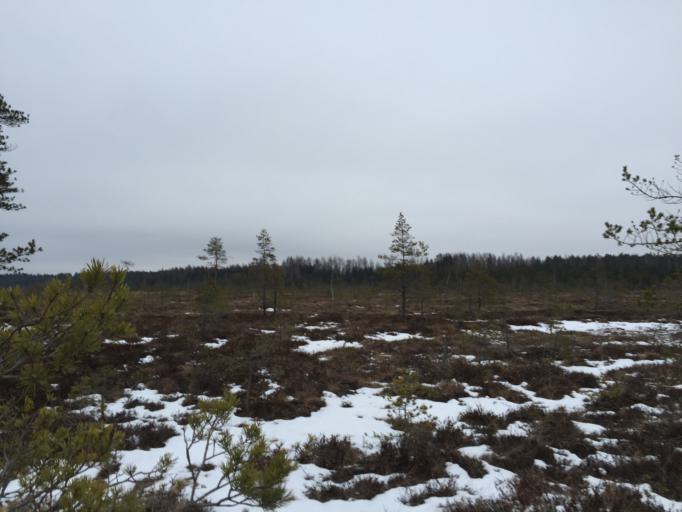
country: LV
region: Saulkrastu
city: Saulkrasti
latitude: 57.2345
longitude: 24.5058
